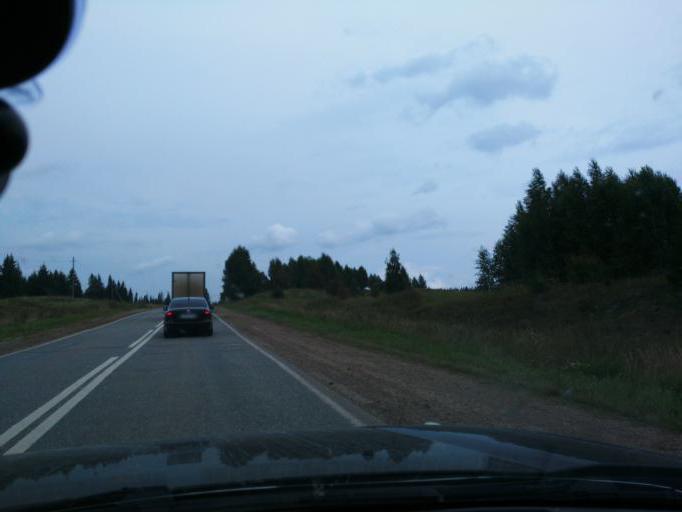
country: RU
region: Bashkortostan
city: Verkhniye Tatyshly
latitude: 56.4946
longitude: 55.8233
